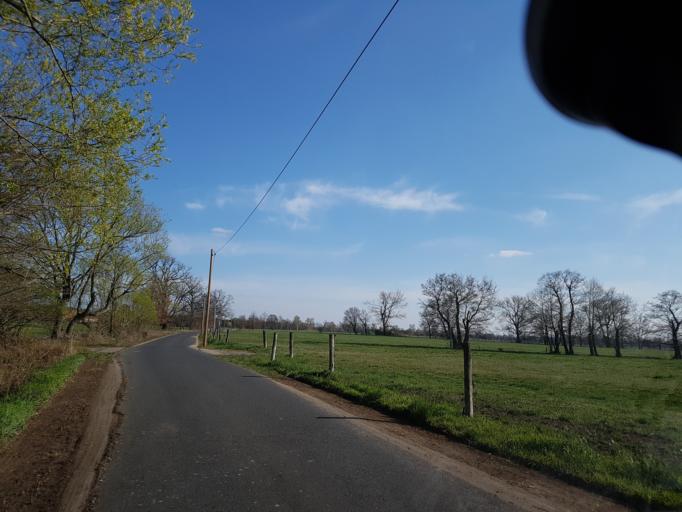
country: DE
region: Brandenburg
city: Schilda
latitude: 51.6303
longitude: 13.3105
